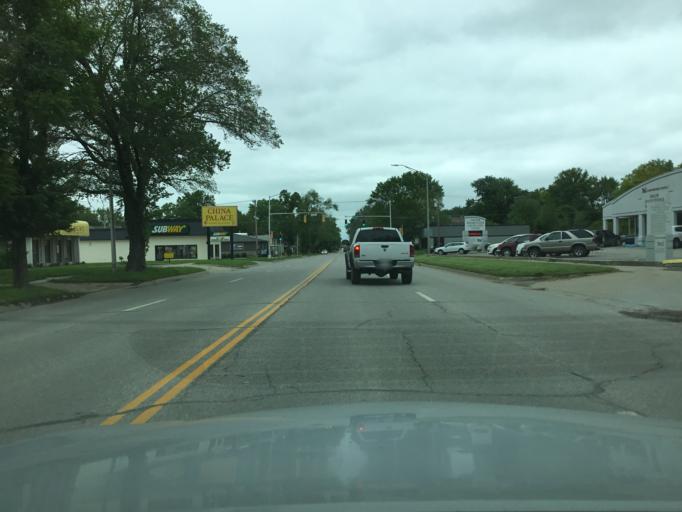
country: US
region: Kansas
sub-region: Franklin County
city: Ottawa
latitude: 38.6039
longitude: -95.2687
